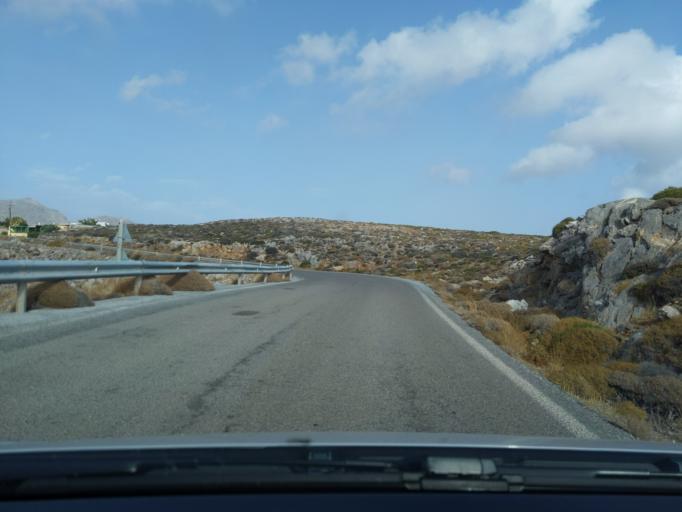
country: GR
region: Crete
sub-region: Nomos Lasithiou
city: Palekastro
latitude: 35.0845
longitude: 26.2582
